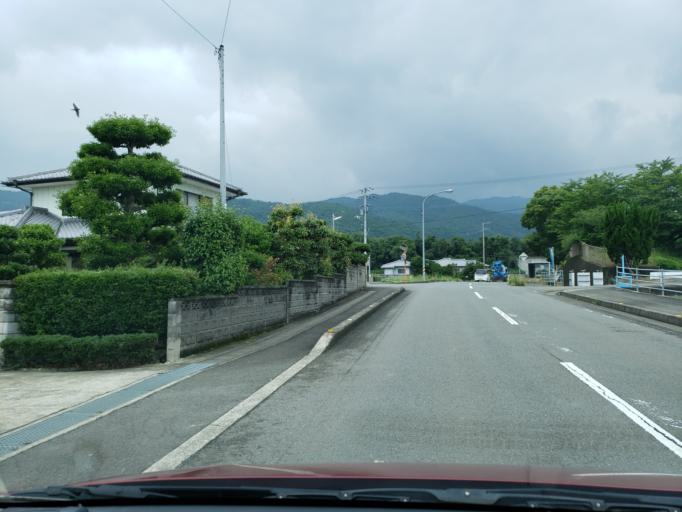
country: JP
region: Tokushima
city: Wakimachi
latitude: 34.0969
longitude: 134.2274
